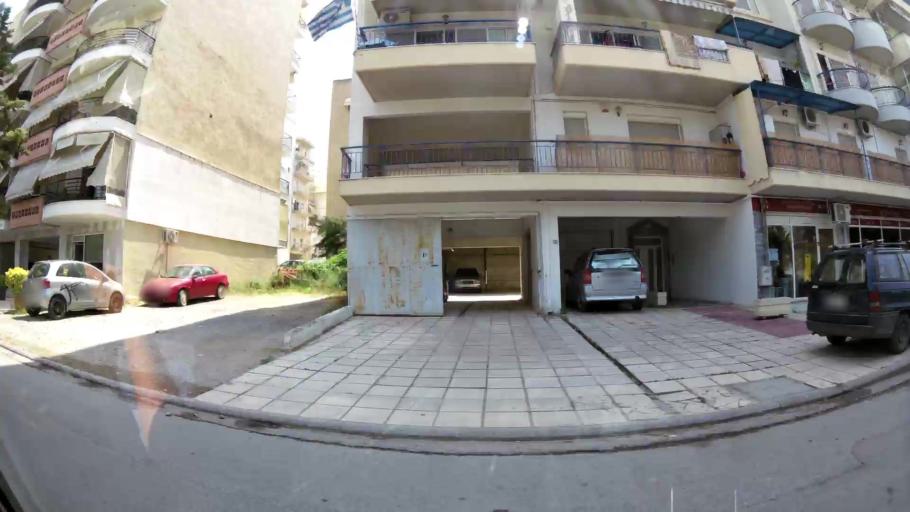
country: GR
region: Central Macedonia
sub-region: Nomos Thessalonikis
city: Evosmos
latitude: 40.6715
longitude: 22.9031
